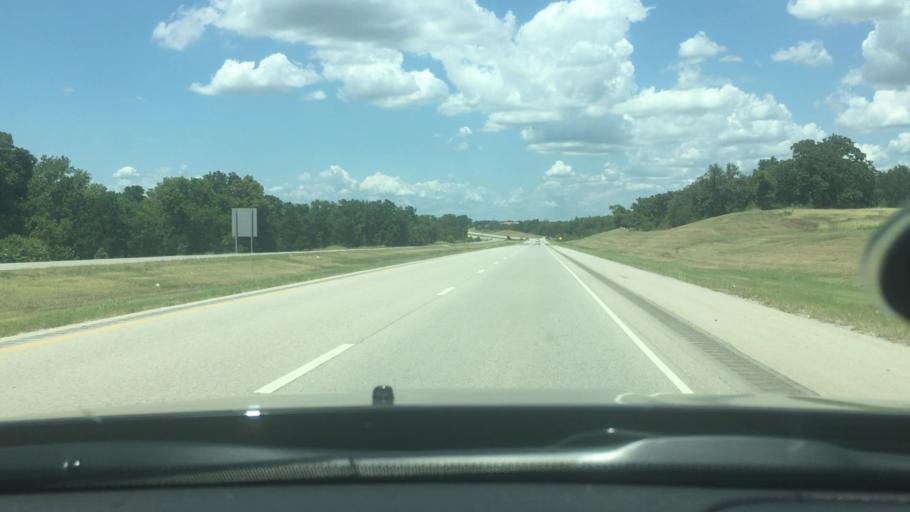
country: US
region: Oklahoma
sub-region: Bryan County
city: Calera
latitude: 33.9834
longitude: -96.4275
